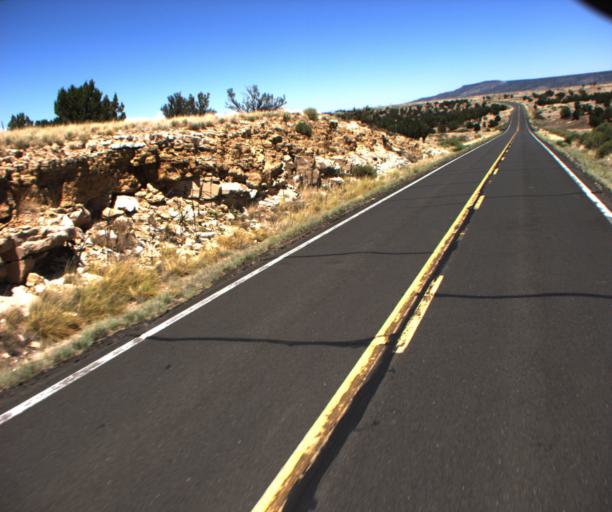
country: US
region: Arizona
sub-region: Coconino County
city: LeChee
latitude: 34.7644
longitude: -111.0155
